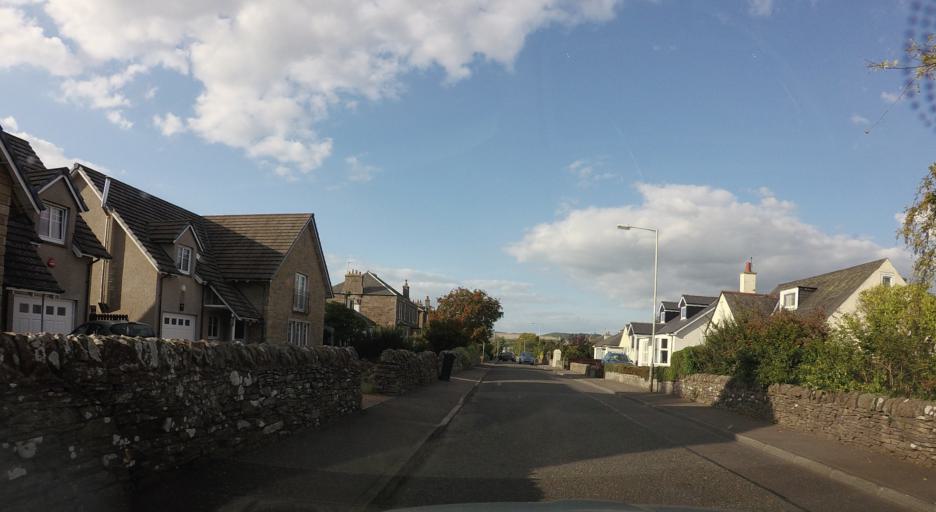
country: GB
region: Scotland
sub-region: Angus
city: Muirhead
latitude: 56.4562
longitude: -3.0628
